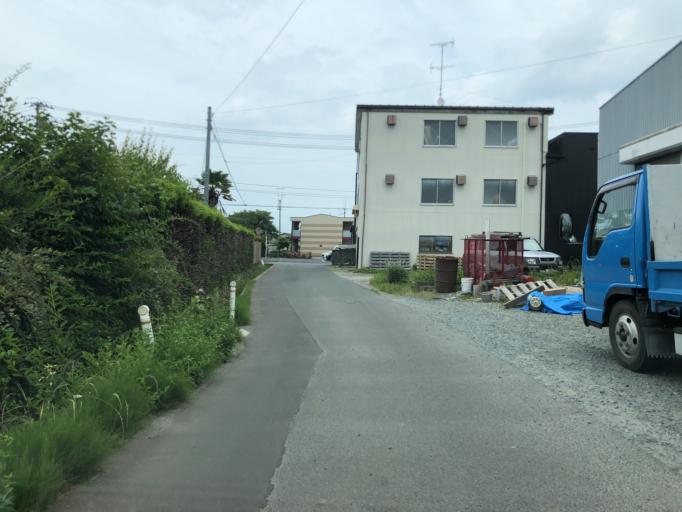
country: JP
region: Miyagi
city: Marumori
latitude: 37.7932
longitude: 140.9240
